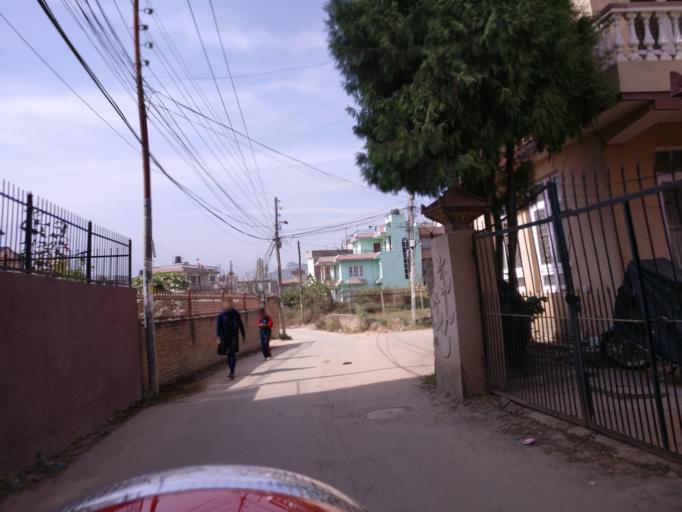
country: NP
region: Central Region
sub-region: Bagmati Zone
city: Patan
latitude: 27.6585
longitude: 85.3125
